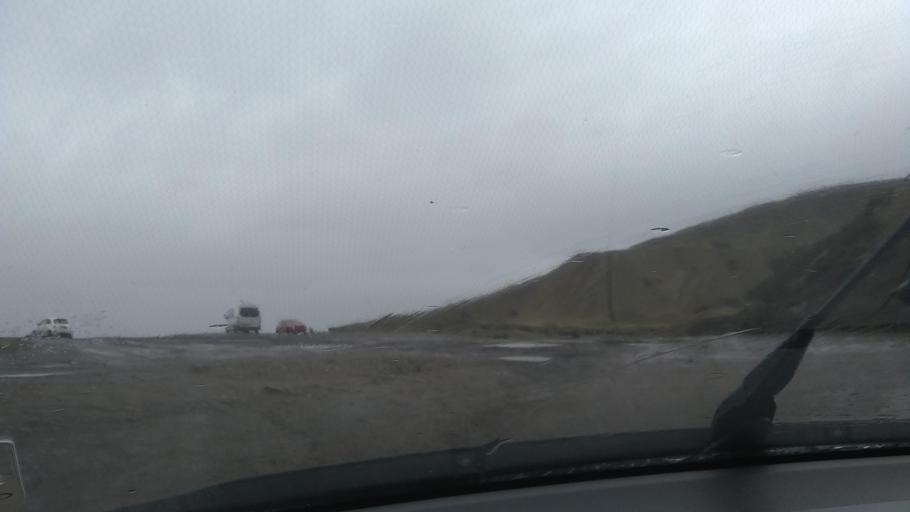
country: GB
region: England
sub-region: Worcestershire
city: Tenbury Wells
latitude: 52.3945
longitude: -2.5979
